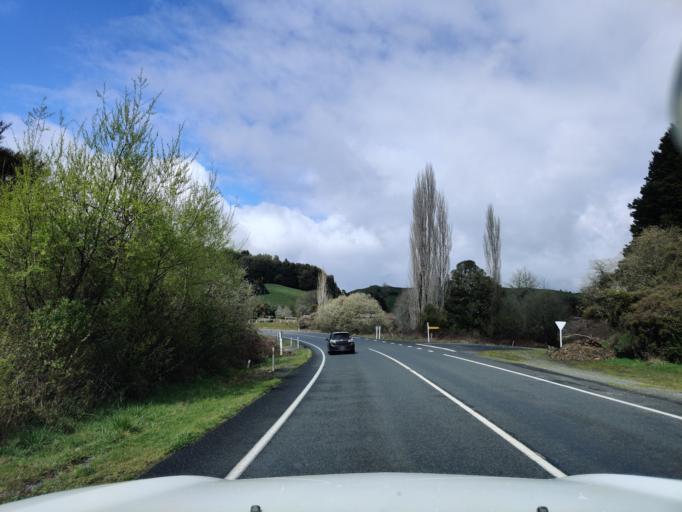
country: NZ
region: Waikato
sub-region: Otorohanga District
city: Otorohanga
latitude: -38.5845
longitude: 175.2154
